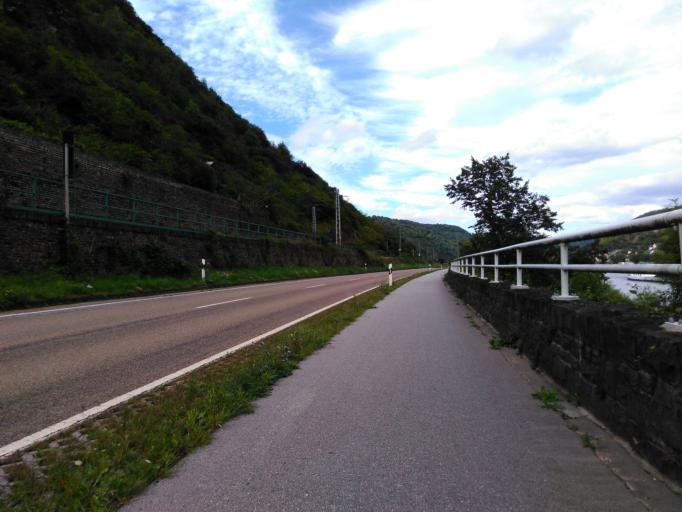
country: DE
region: Rheinland-Pfalz
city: Moselkern
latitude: 50.2035
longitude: 7.3769
